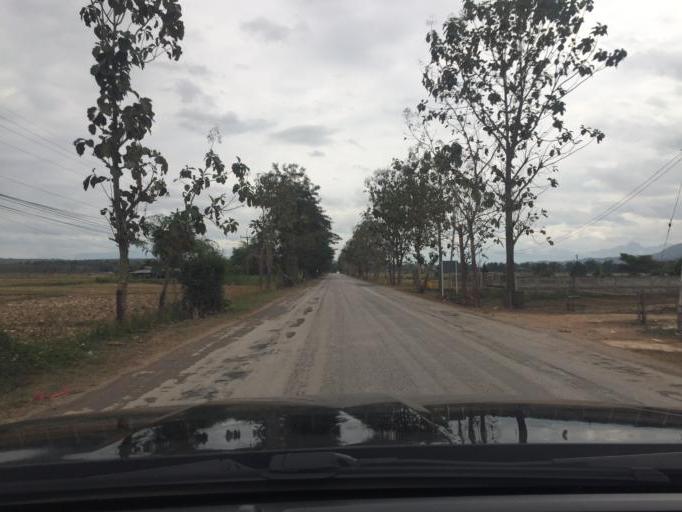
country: TH
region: Phayao
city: Pong
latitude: 19.1669
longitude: 100.2917
